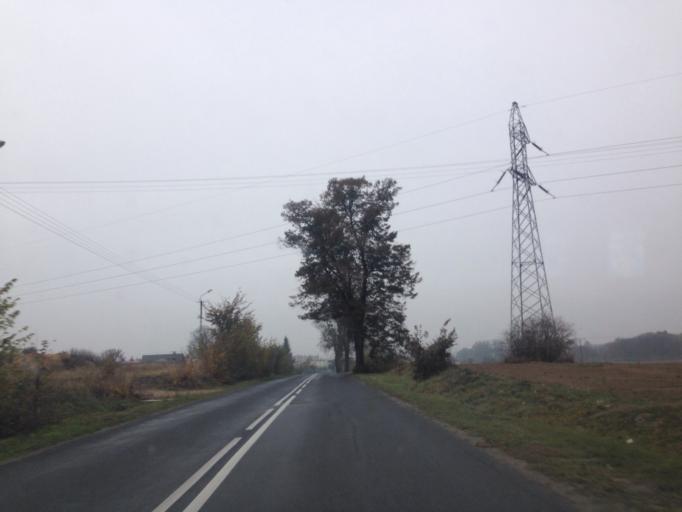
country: PL
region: Kujawsko-Pomorskie
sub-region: Powiat brodnicki
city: Brodnica
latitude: 53.2430
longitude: 19.4735
